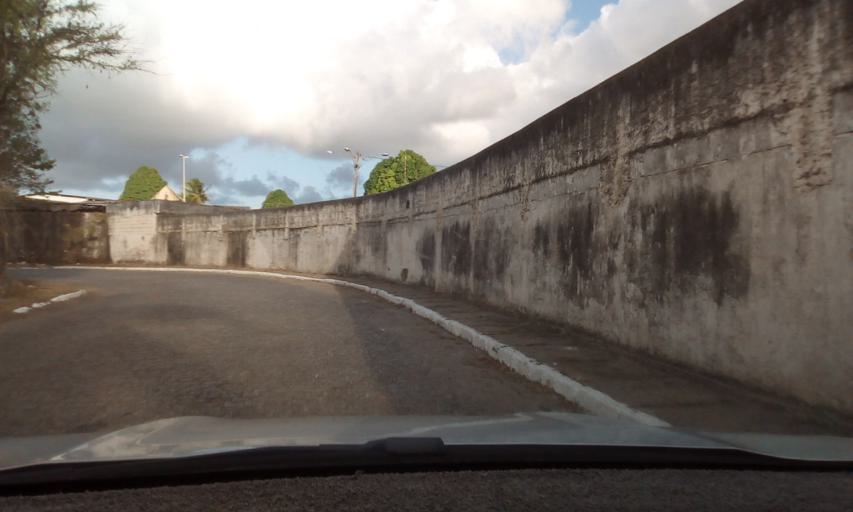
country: BR
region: Paraiba
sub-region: Bayeux
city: Bayeux
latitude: -7.1483
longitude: -34.8941
